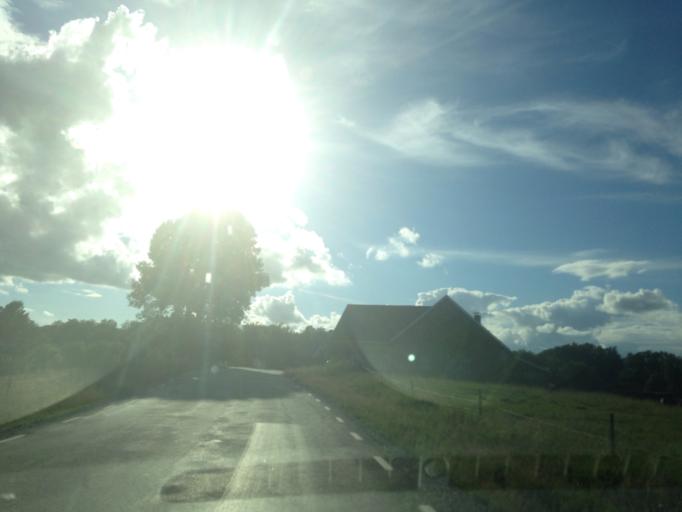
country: SE
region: Vaestra Goetaland
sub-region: Marks Kommun
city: Horred
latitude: 57.4724
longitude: 12.4543
